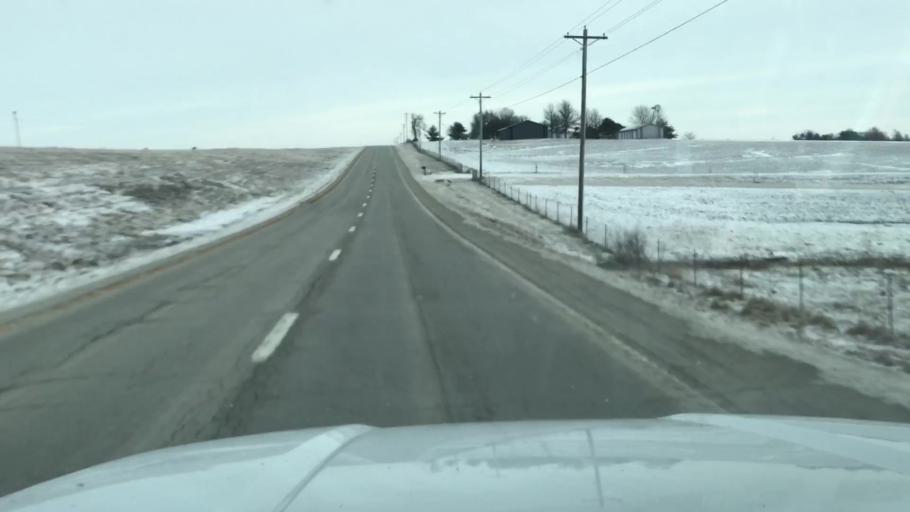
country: US
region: Missouri
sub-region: Andrew County
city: Savannah
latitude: 39.9894
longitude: -94.8799
